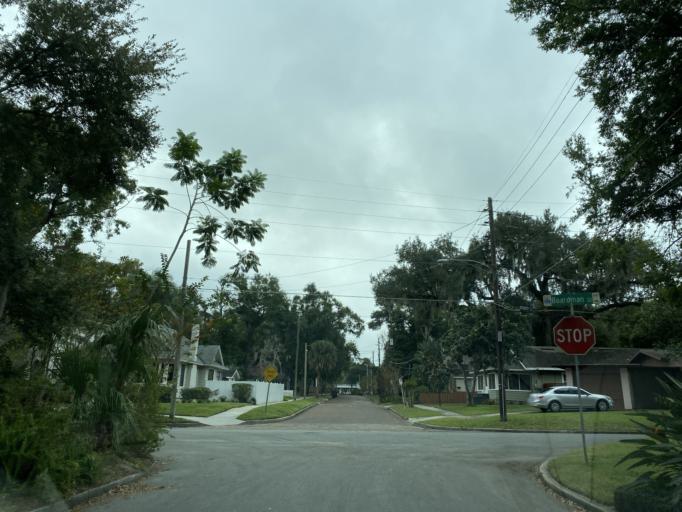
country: US
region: Florida
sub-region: Orange County
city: Orlando
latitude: 28.5549
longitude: -81.3889
